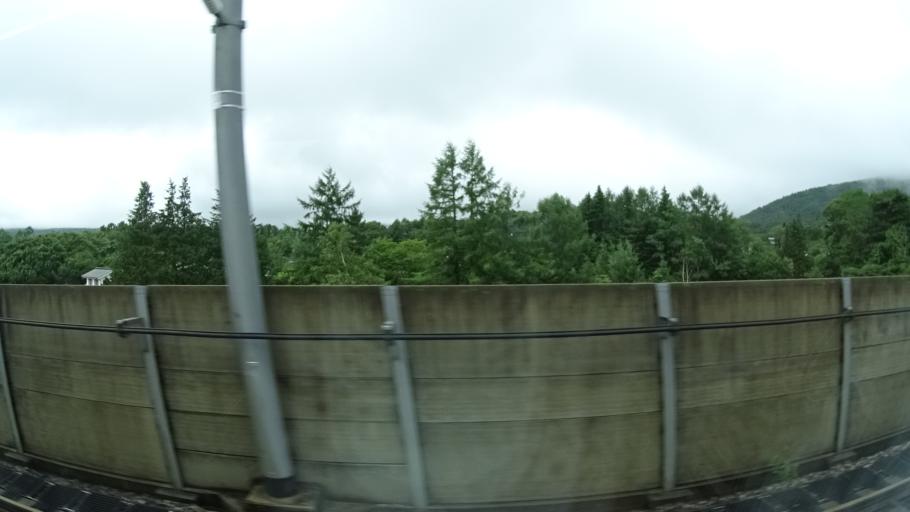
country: JP
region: Nagano
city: Komoro
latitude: 36.3410
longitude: 138.5924
